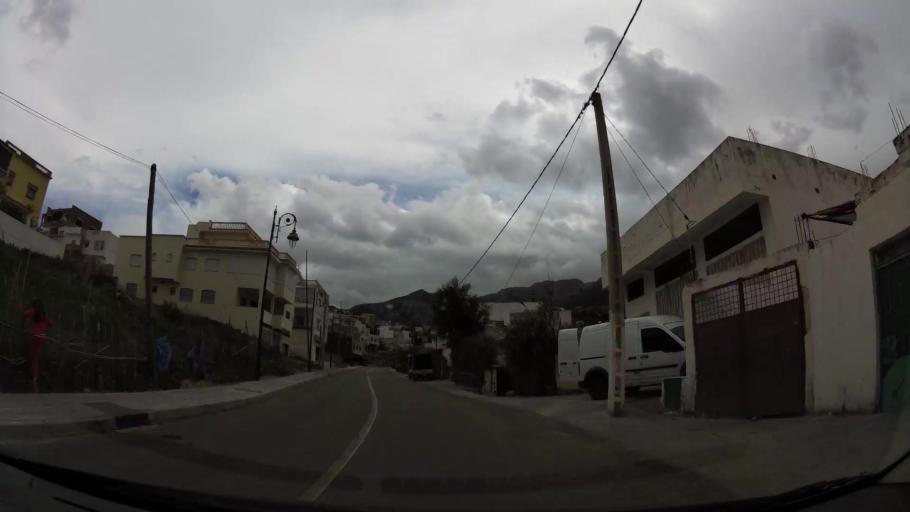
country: MA
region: Tanger-Tetouan
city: Tetouan
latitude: 35.5525
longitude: -5.3603
